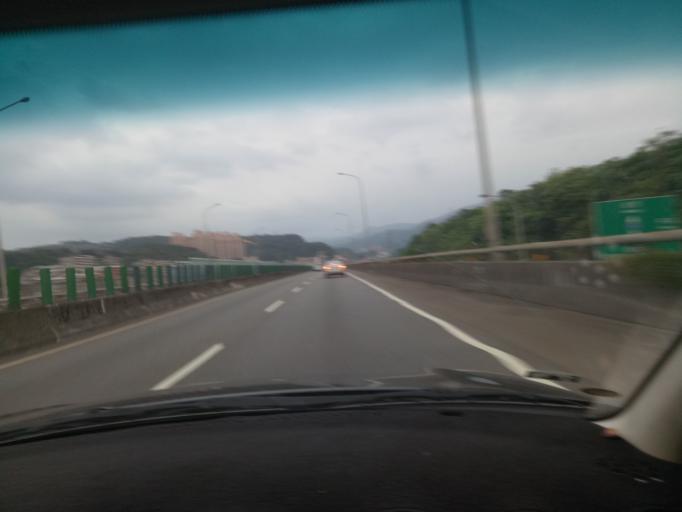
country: TW
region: Taiwan
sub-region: Keelung
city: Keelung
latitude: 25.1051
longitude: 121.7327
